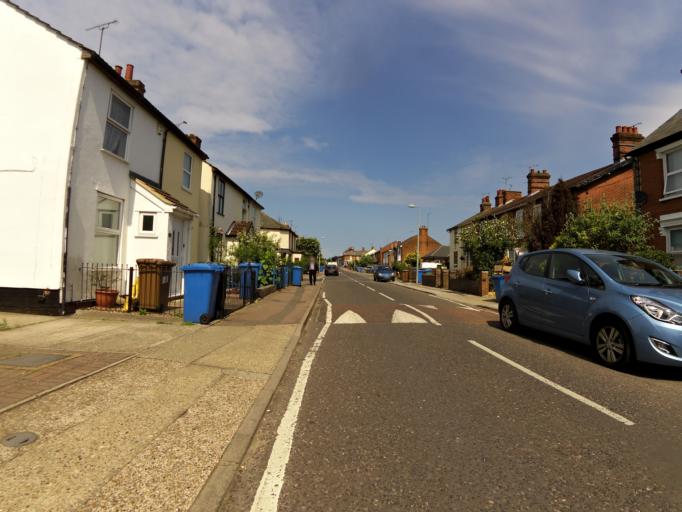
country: GB
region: England
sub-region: Suffolk
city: Ipswich
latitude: 52.0656
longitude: 1.1349
